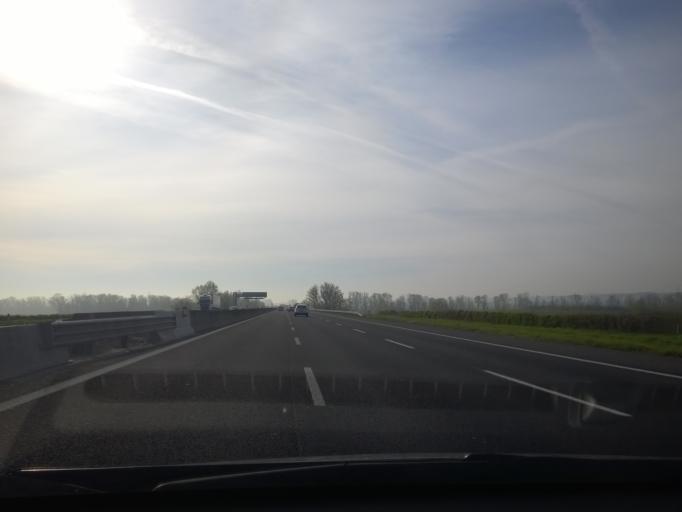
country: IT
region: Emilia-Romagna
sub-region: Provincia di Bologna
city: Castel San Pietro Terme
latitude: 44.4207
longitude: 11.6202
